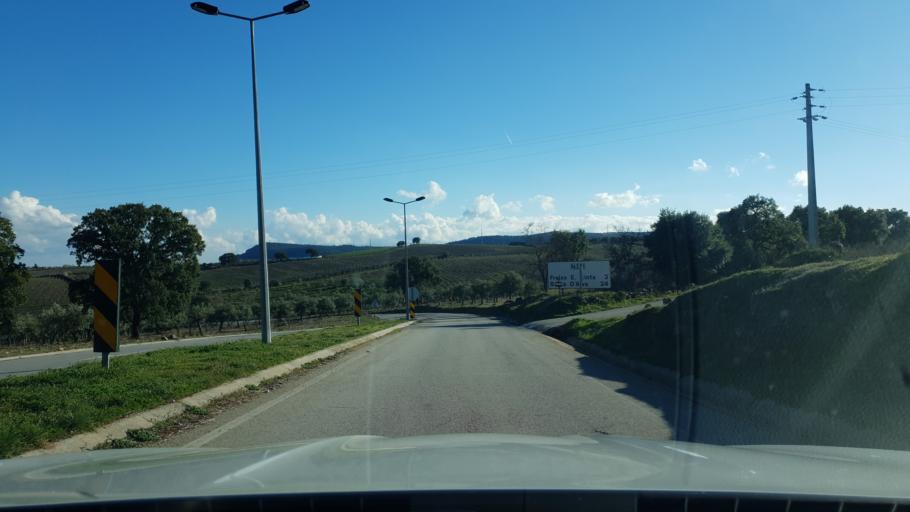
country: PT
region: Braganca
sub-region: Freixo de Espada A Cinta
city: Freixo de Espada a Cinta
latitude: 41.0954
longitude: -6.8320
